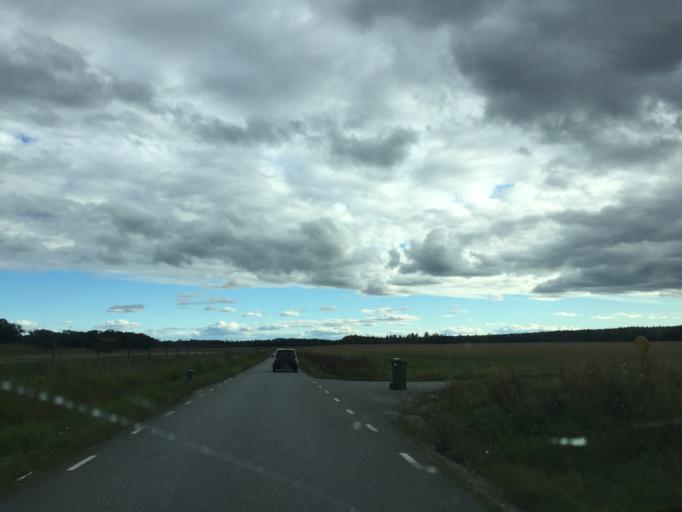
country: SE
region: OErebro
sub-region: Orebro Kommun
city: Hovsta
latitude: 59.3522
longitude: 15.1637
